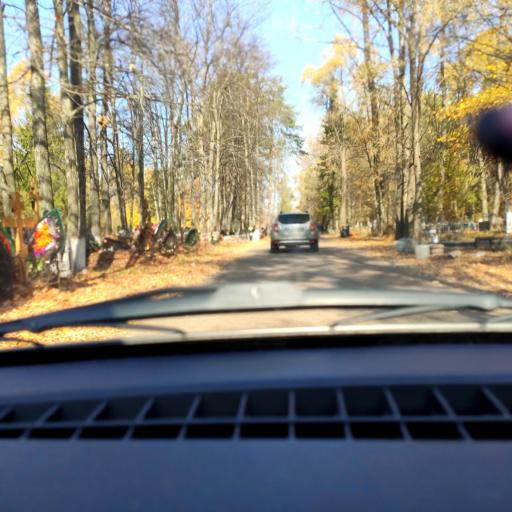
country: RU
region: Bashkortostan
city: Mikhaylovka
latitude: 54.8092
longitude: 55.8633
